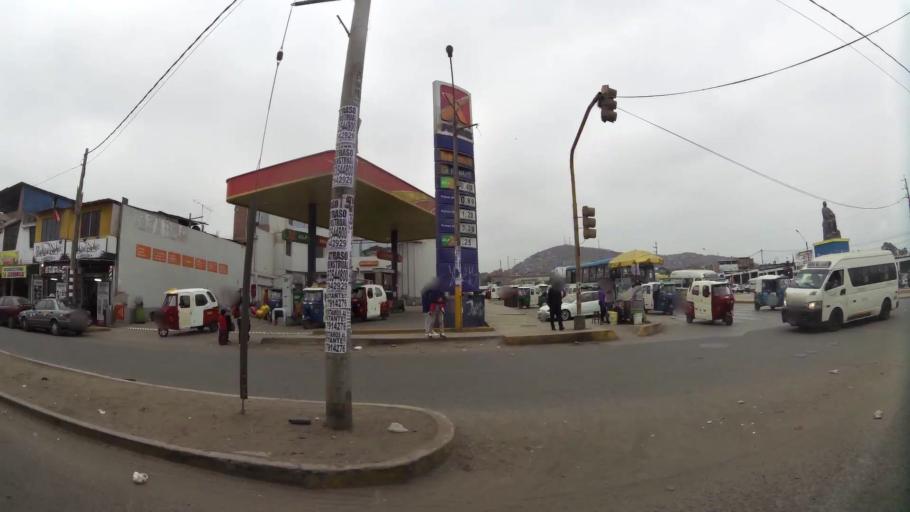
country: PE
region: Lima
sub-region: Lima
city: Surco
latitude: -12.2118
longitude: -76.9345
